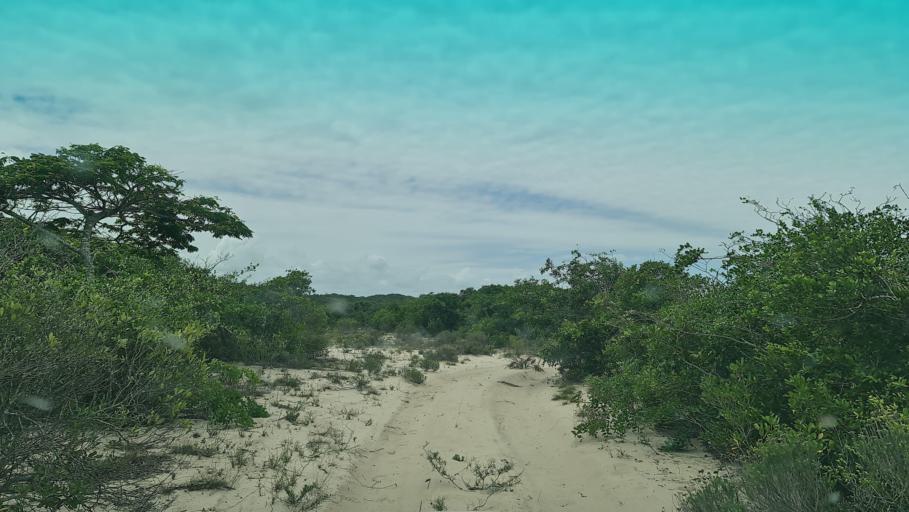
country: MZ
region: Maputo
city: Manhica
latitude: -25.6356
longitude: 32.7851
